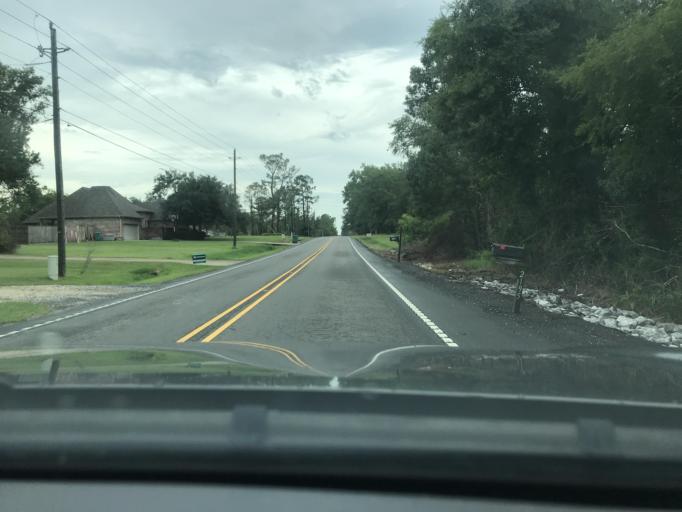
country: US
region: Louisiana
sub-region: Calcasieu Parish
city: Moss Bluff
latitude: 30.3359
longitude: -93.2580
